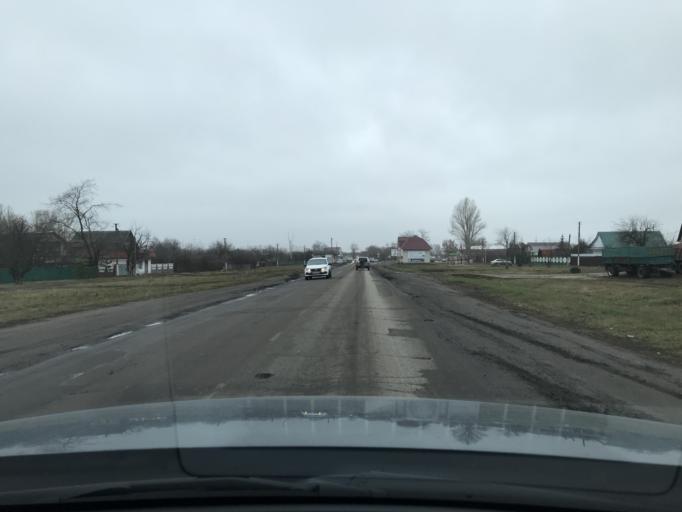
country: RU
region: Penza
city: Zemetchino
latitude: 53.5023
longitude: 42.6319
